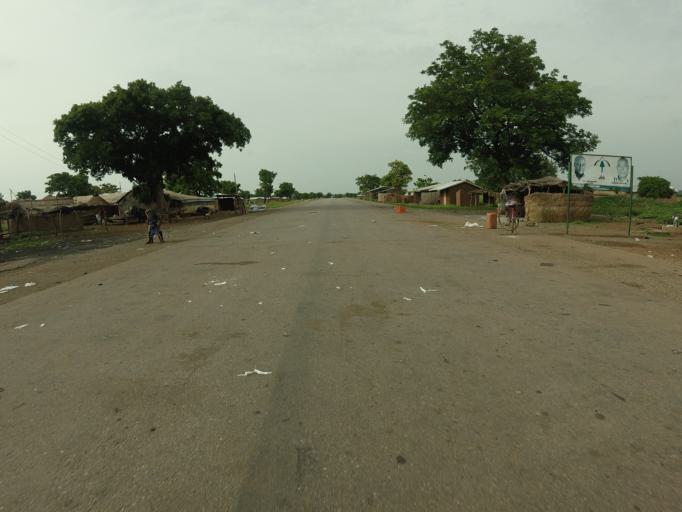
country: GH
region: Northern
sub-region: Yendi
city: Yendi
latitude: 9.8107
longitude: -0.1149
